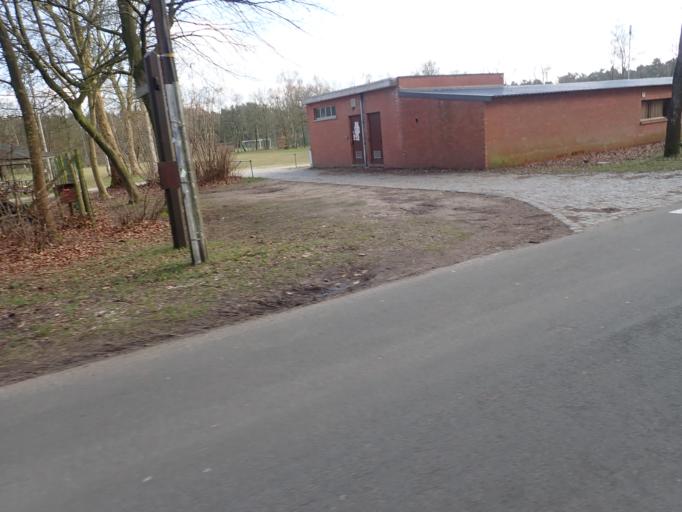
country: BE
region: Flanders
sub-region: Provincie Antwerpen
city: Lille
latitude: 51.2493
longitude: 4.8586
